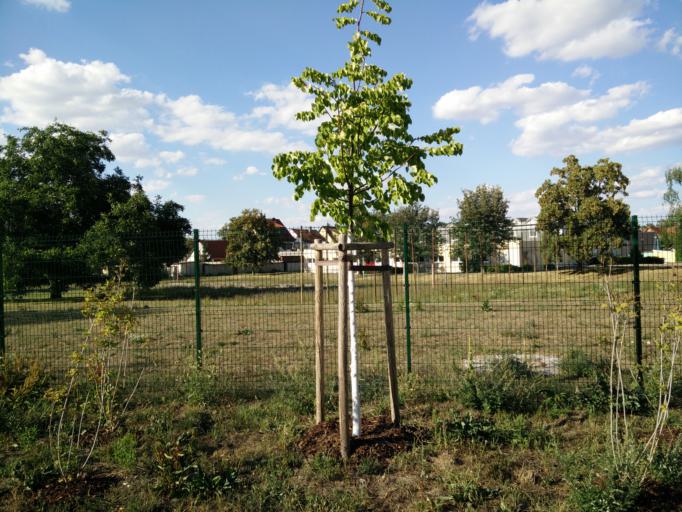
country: DE
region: Thuringia
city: Noda
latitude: 51.0189
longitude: 10.9933
